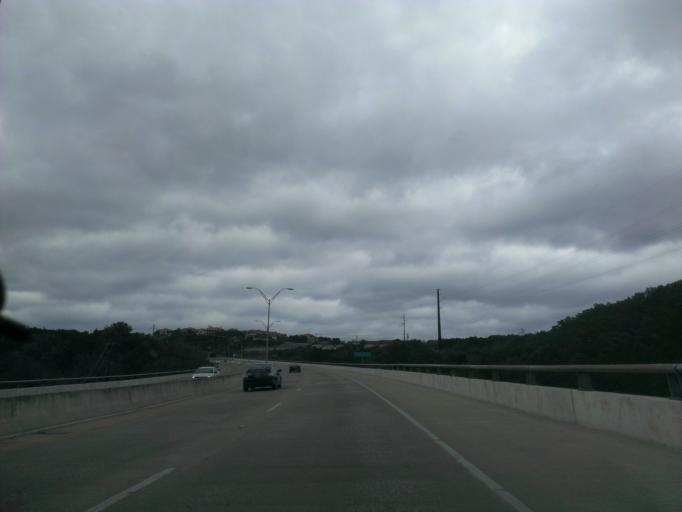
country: US
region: Texas
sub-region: Travis County
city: Hudson Bend
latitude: 30.3935
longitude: -97.9112
